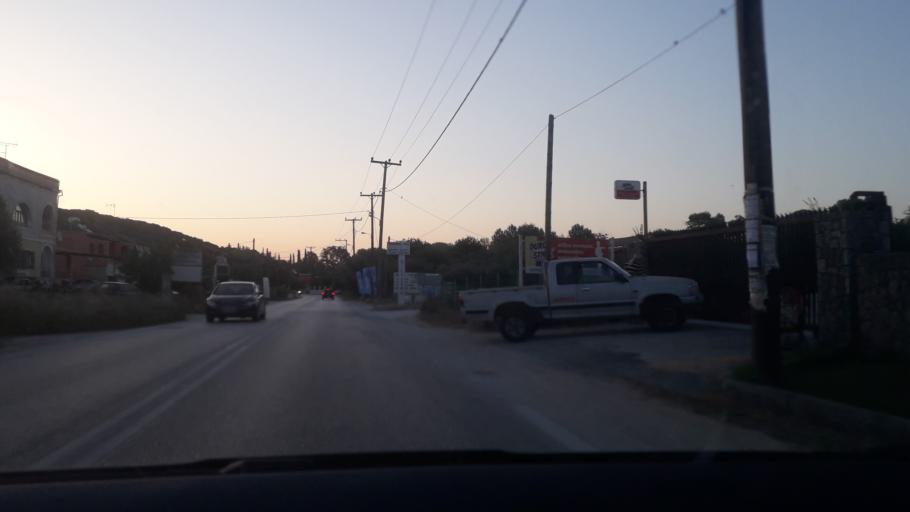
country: GR
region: Ionian Islands
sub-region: Nomos Kerkyras
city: Agios Matthaios
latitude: 39.4772
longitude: 19.9142
